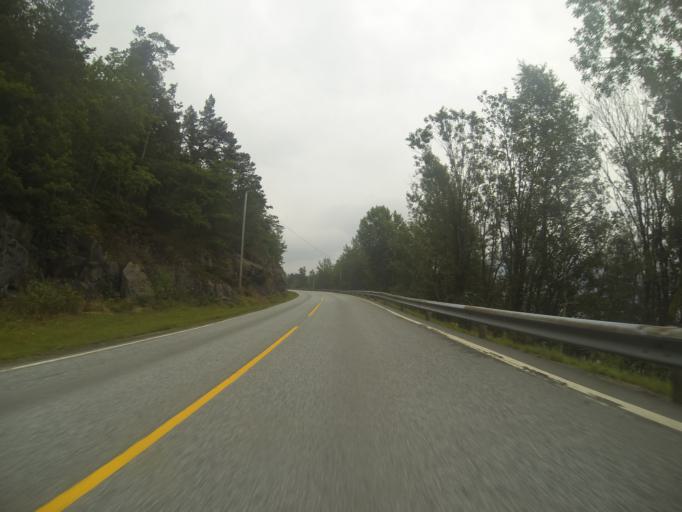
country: NO
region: Rogaland
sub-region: Suldal
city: Sand
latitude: 59.5107
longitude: 6.2186
